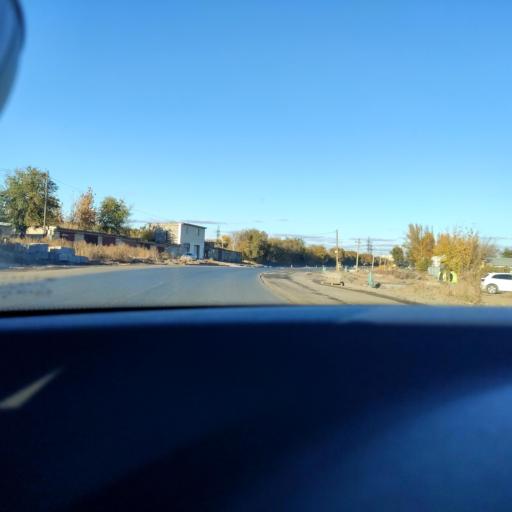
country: RU
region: Samara
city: Samara
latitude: 53.1863
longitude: 50.2196
